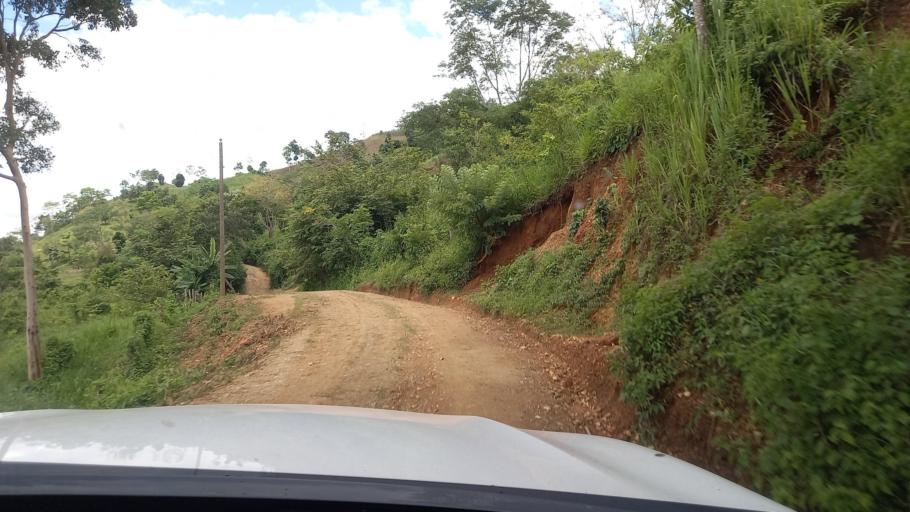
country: NI
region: Nueva Segovia
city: Wiwili
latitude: 13.7334
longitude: -85.7885
